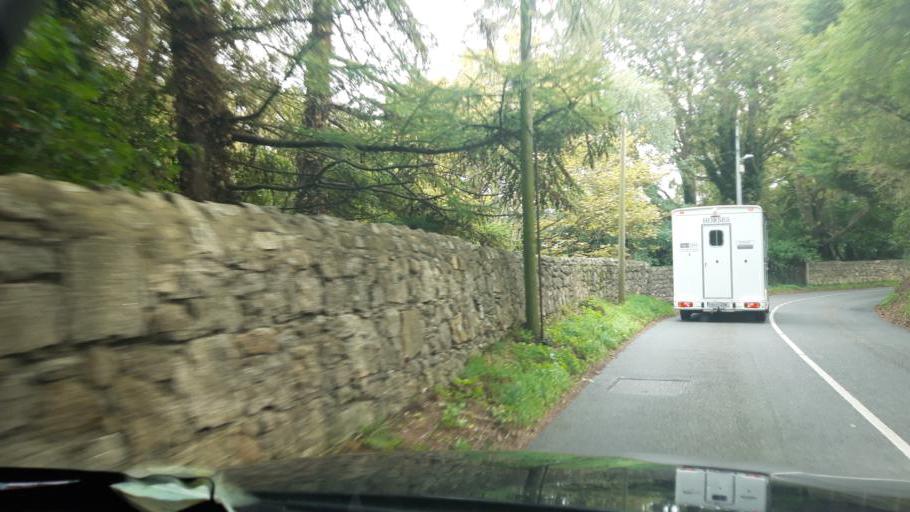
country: IE
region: Leinster
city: Foxrock
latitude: 53.2337
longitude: -6.1998
